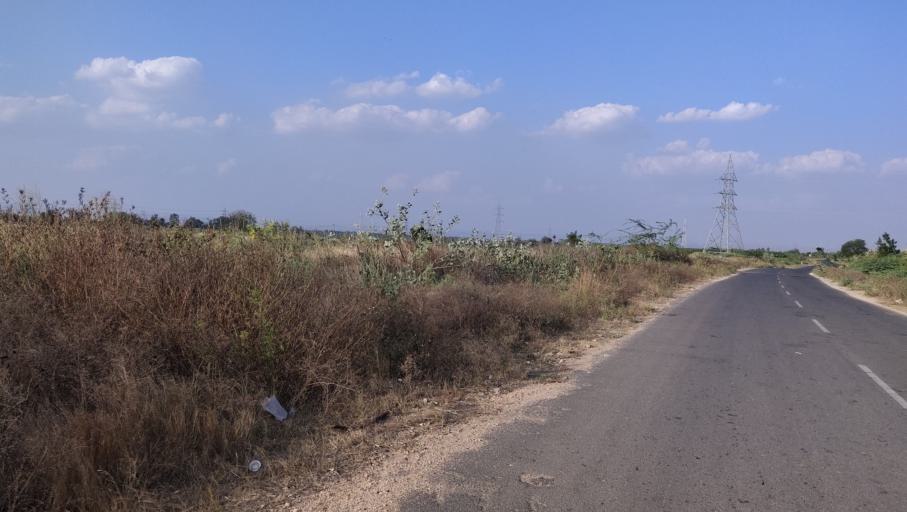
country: IN
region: Andhra Pradesh
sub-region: Anantapur
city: Tadpatri
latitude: 14.9483
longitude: 77.8786
